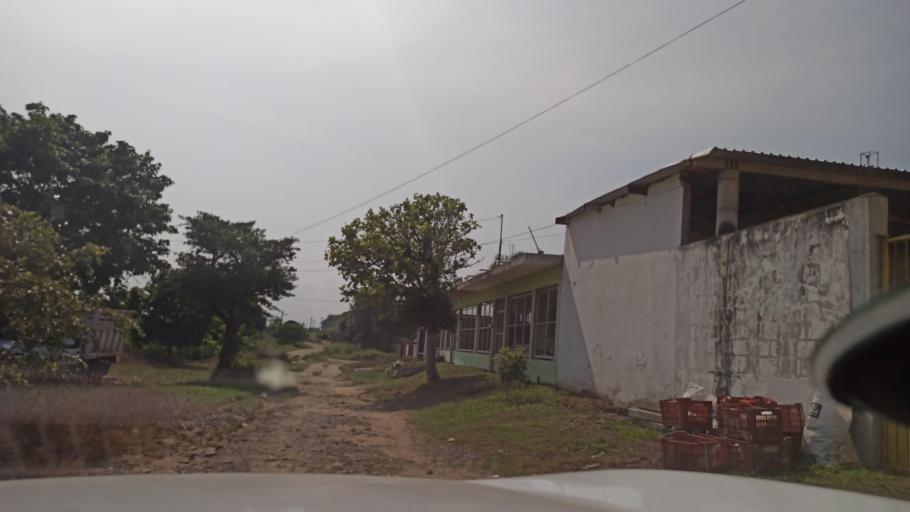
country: MX
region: Veracruz
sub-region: Martinez de la Torre
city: El Progreso
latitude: 20.1483
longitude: -97.0643
